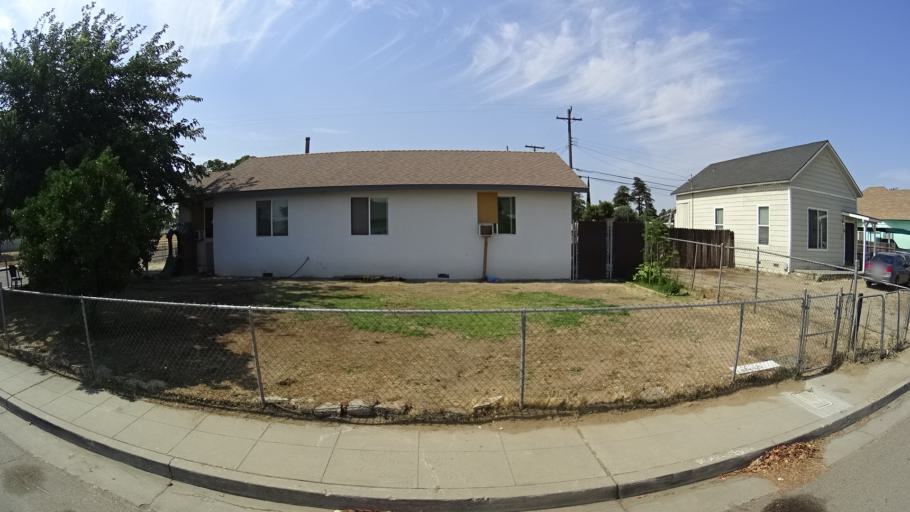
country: US
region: California
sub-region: Fresno County
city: West Park
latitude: 36.7523
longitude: -119.8288
